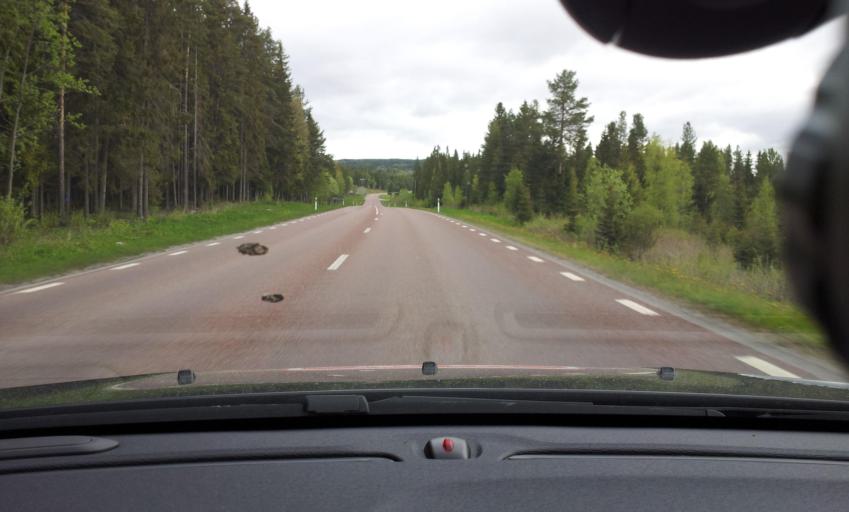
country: SE
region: Jaemtland
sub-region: OEstersunds Kommun
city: Brunflo
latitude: 63.0587
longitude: 14.8338
